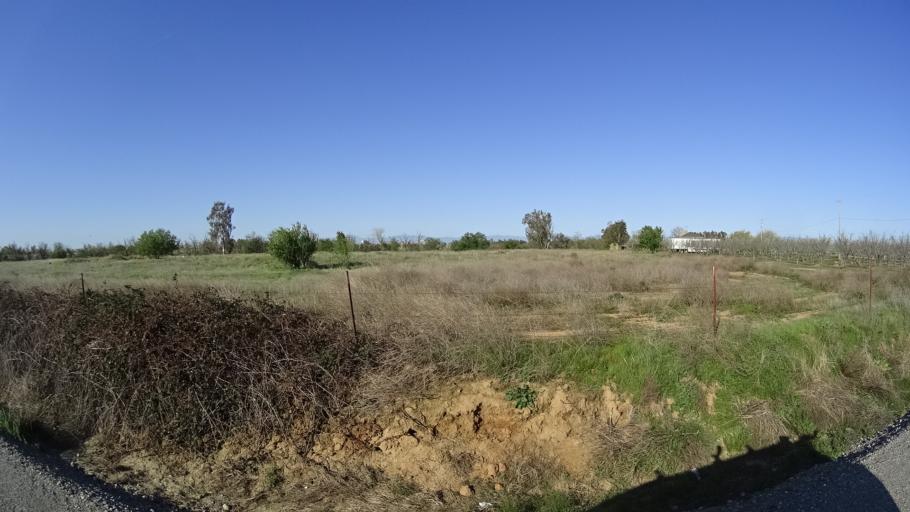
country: US
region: California
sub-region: Glenn County
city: Hamilton City
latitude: 39.7530
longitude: -122.1016
